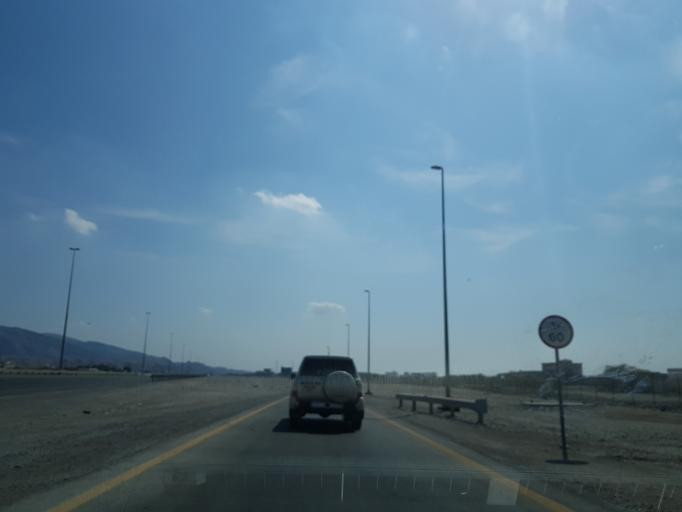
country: AE
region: Ra's al Khaymah
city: Ras al-Khaimah
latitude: 25.8030
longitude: 56.0301
